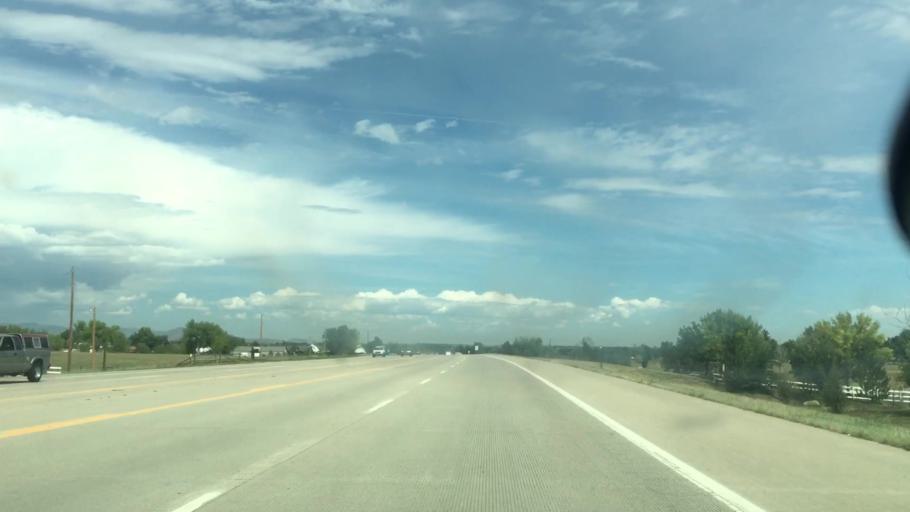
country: US
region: Colorado
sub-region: Larimer County
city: Berthoud
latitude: 40.2571
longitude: -105.1024
